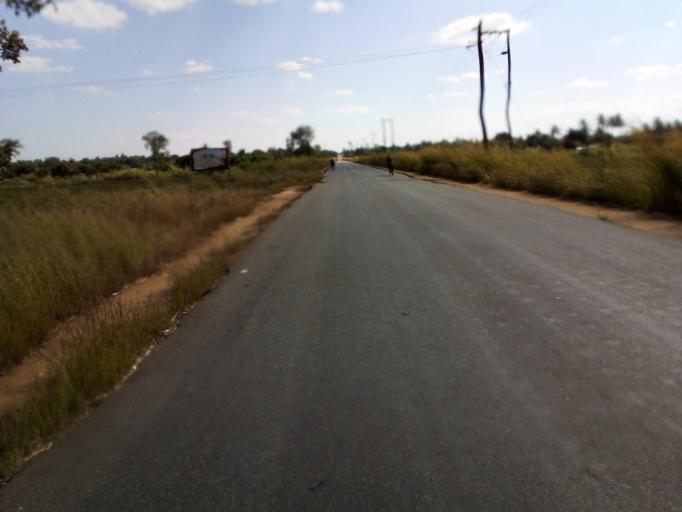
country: MZ
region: Zambezia
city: Quelimane
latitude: -17.5779
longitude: 36.6812
